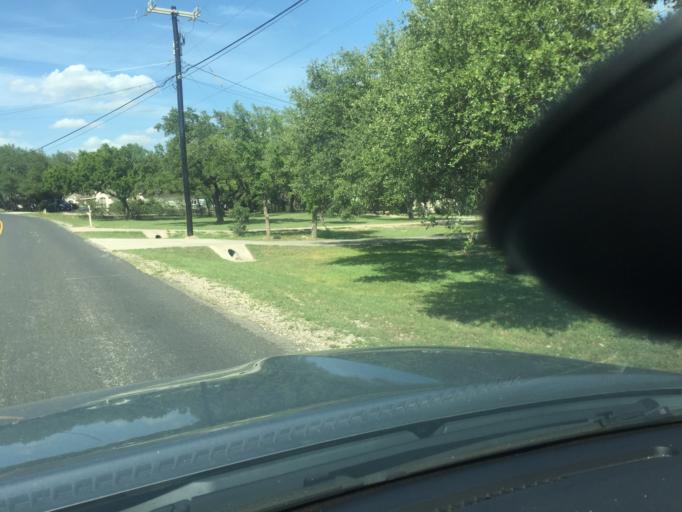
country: US
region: Texas
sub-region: Bexar County
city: Timberwood Park
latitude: 29.6854
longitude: -98.4827
